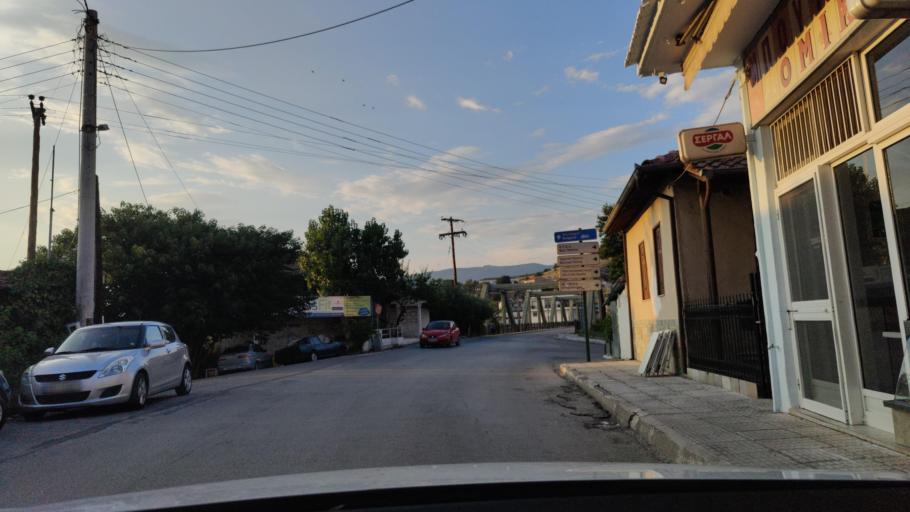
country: GR
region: Central Macedonia
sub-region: Nomos Serron
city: Sidirokastro
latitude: 41.2369
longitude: 23.3905
